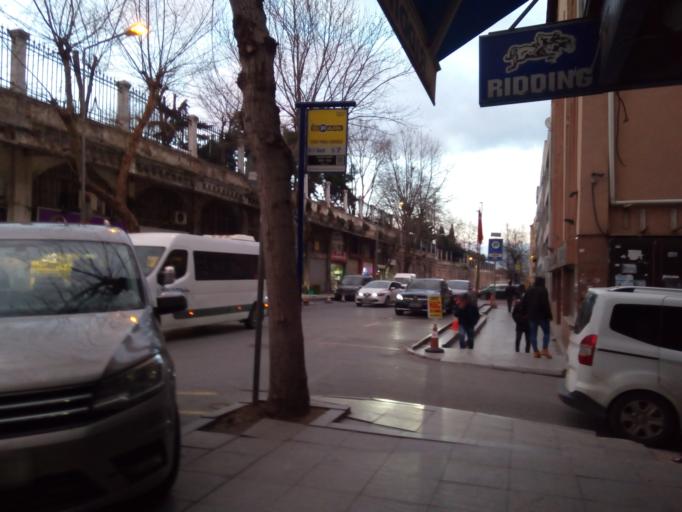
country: TR
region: Istanbul
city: Eminoenue
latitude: 41.0130
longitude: 28.9659
